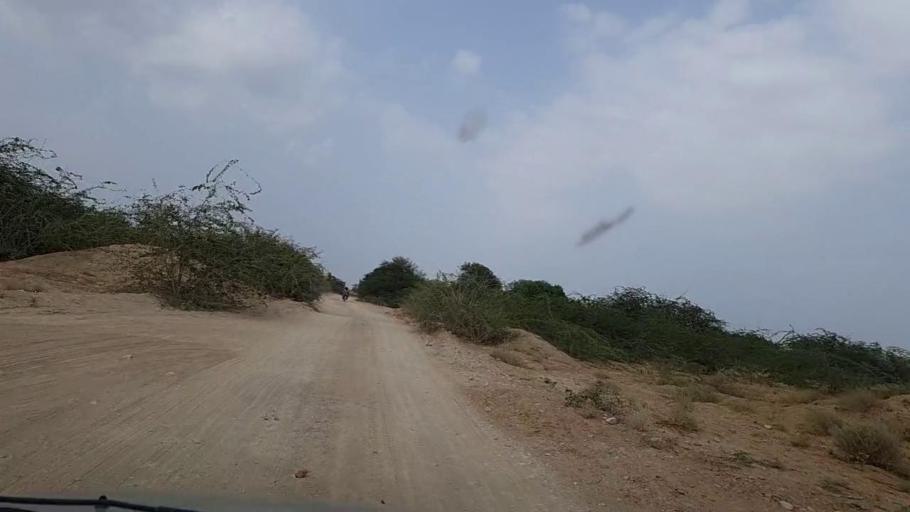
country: PK
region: Sindh
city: Kotri
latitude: 25.2809
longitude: 68.2575
